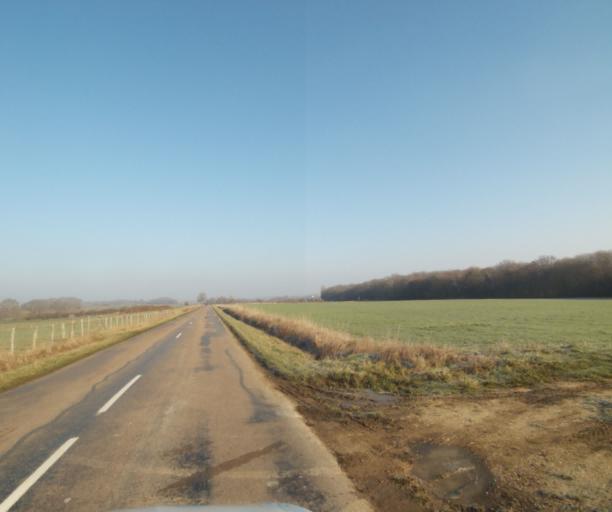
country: FR
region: Champagne-Ardenne
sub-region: Departement de la Haute-Marne
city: Montier-en-Der
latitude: 48.4370
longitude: 4.7551
